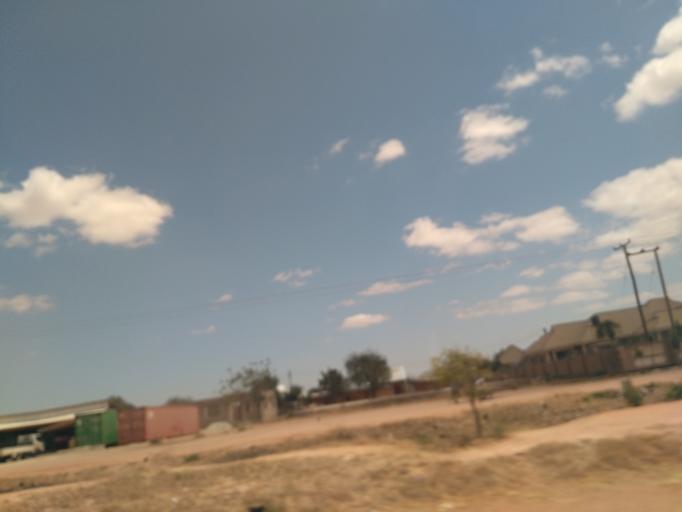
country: TZ
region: Dodoma
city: Kisasa
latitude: -6.1618
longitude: 35.7920
